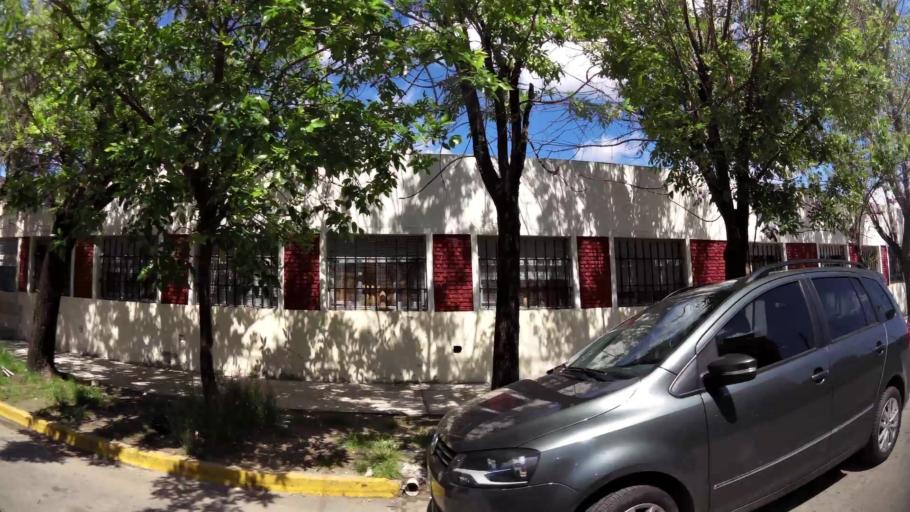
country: AR
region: Buenos Aires F.D.
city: Villa Lugano
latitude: -34.6858
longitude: -58.4351
